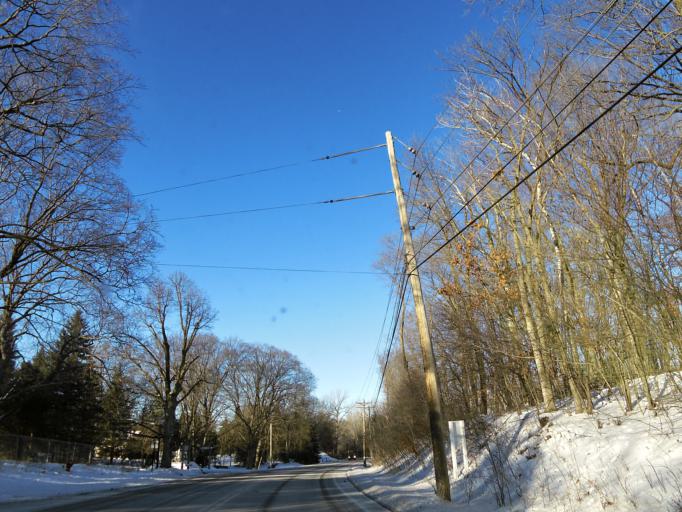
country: US
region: Minnesota
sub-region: Hennepin County
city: Mound
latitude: 44.9024
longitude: -93.6782
